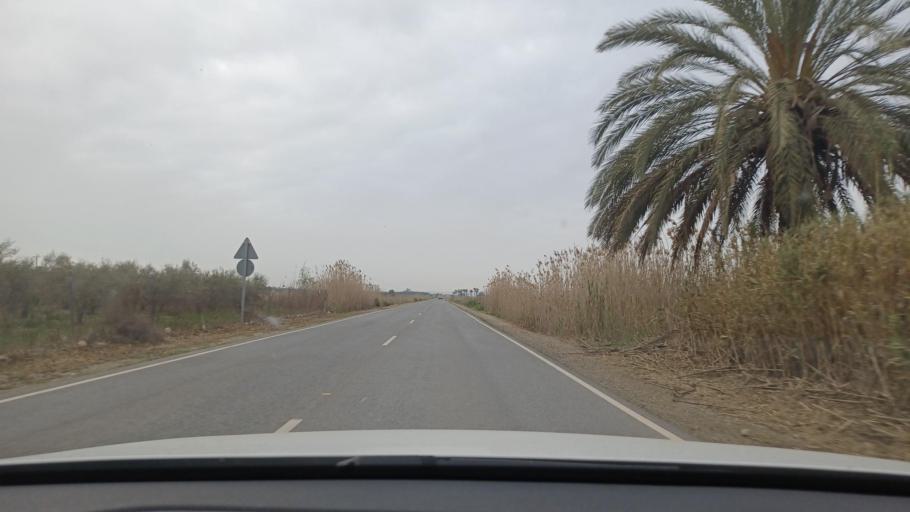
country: ES
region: Valencia
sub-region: Provincia de Alicante
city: Daya Vieja
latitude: 38.1654
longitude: -0.7027
